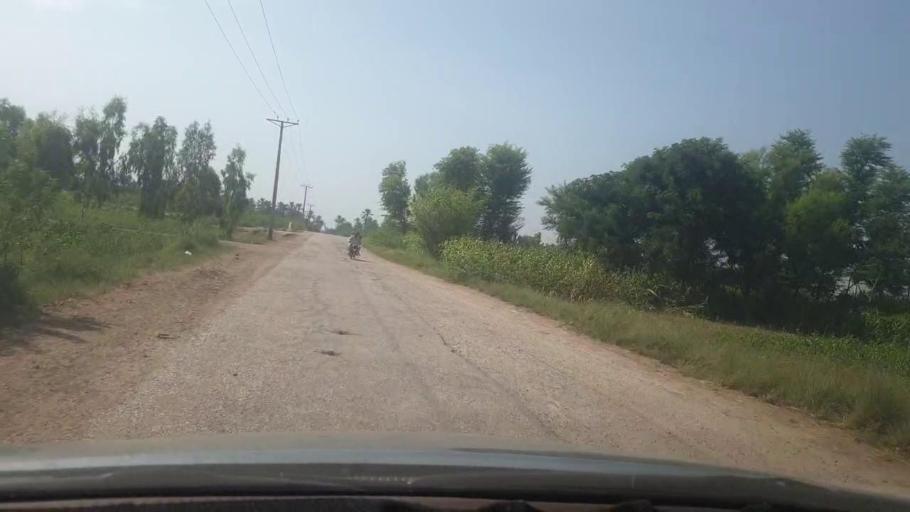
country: PK
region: Sindh
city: Gambat
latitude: 27.3288
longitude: 68.5504
